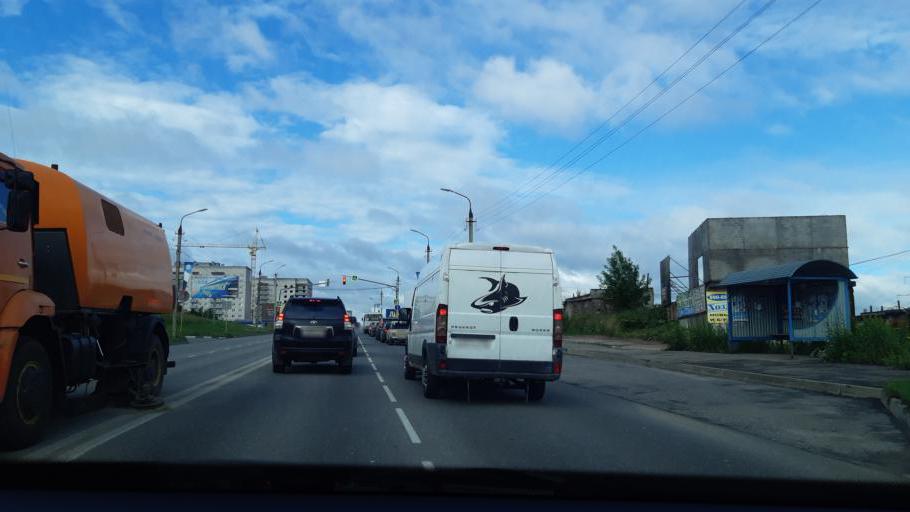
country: RU
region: Smolensk
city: Smolensk
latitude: 54.7595
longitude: 32.0808
